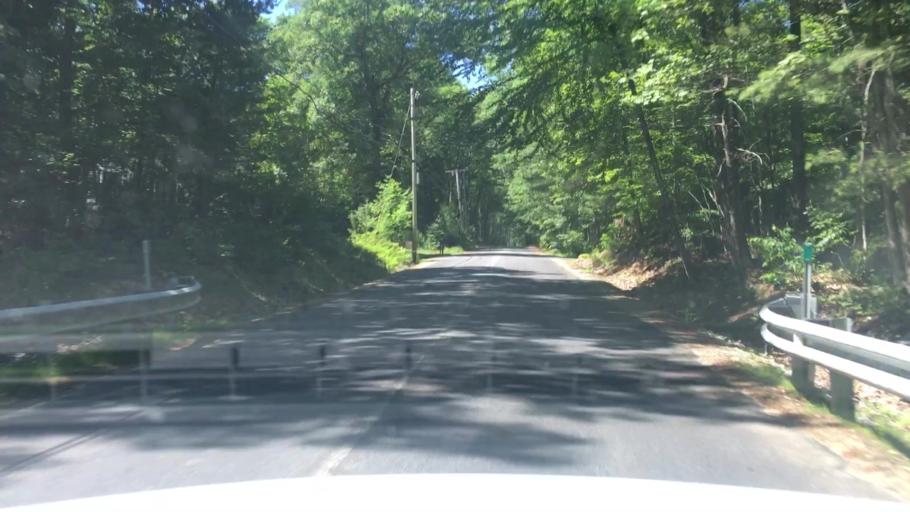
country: US
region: New Hampshire
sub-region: Merrimack County
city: Hopkinton
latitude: 43.2368
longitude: -71.6372
